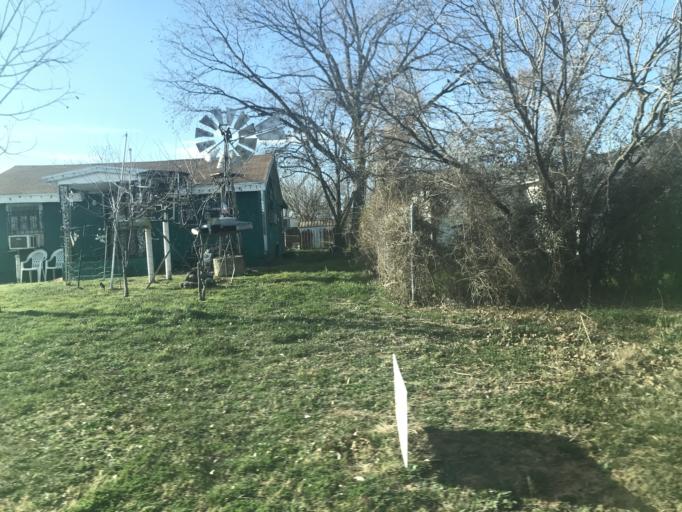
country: US
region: Texas
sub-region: Tom Green County
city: San Angelo
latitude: 31.4372
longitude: -100.4454
